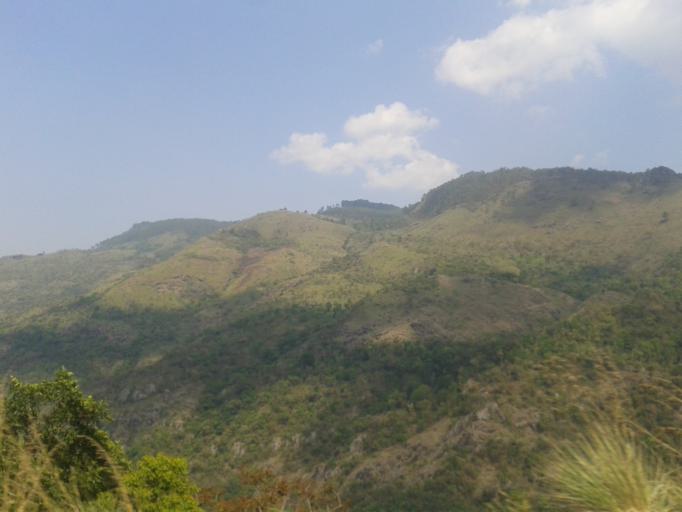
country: IN
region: Tamil Nadu
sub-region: Dindigul
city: Ayakudi
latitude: 10.3421
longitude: 77.5744
